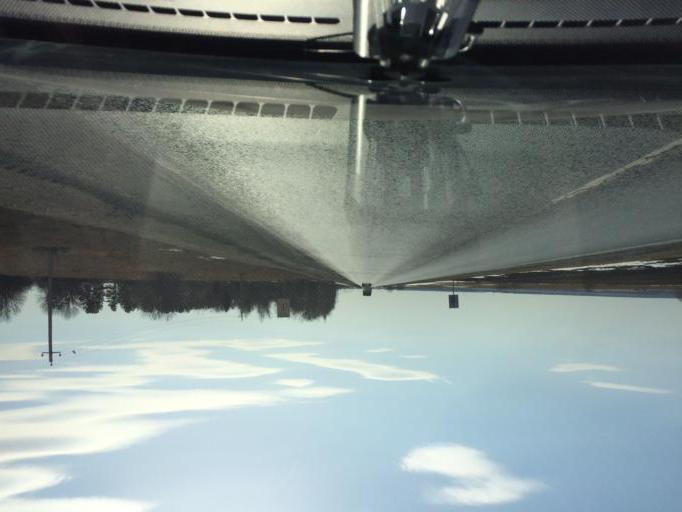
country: RU
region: Mariy-El
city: Yoshkar-Ola
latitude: 56.7048
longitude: 48.0752
